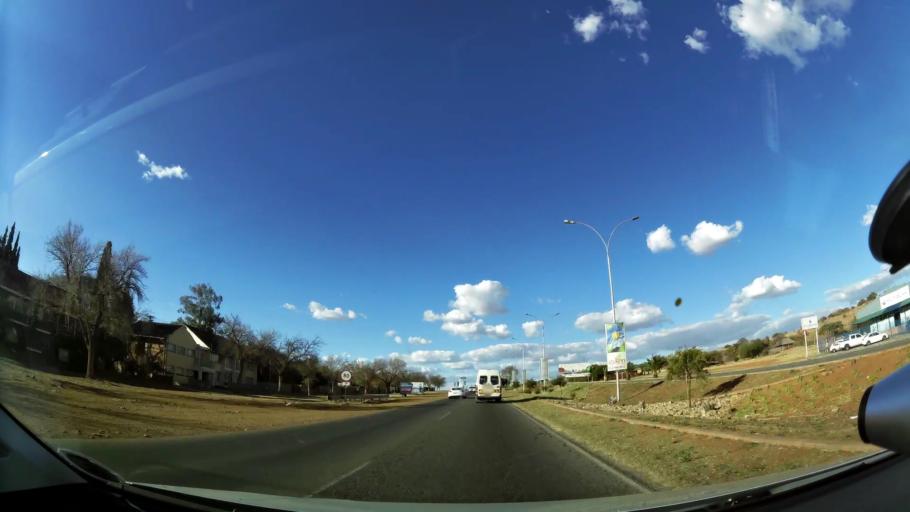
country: ZA
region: North-West
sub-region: Dr Kenneth Kaunda District Municipality
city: Klerksdorp
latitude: -26.8535
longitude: 26.6836
